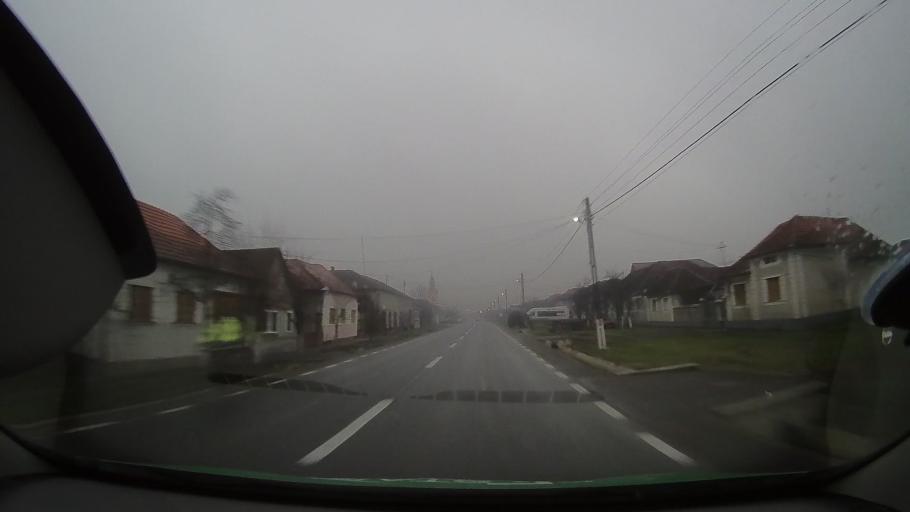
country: RO
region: Bihor
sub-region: Comuna Olcea
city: Calacea
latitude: 46.6392
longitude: 21.9559
